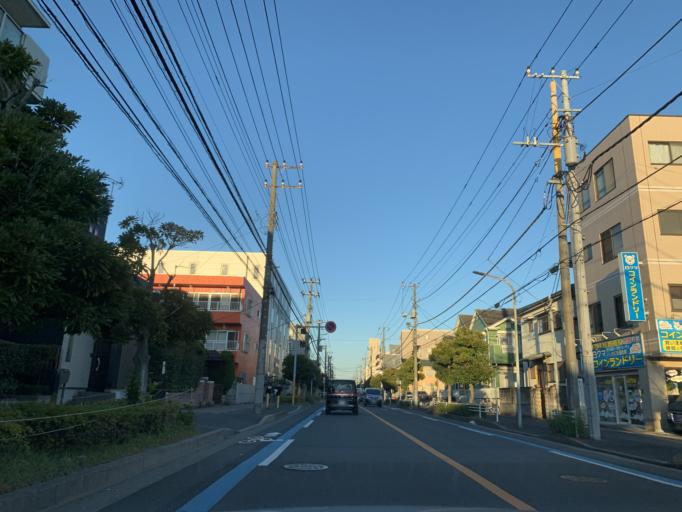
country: JP
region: Tokyo
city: Urayasu
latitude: 35.6816
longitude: 139.9230
